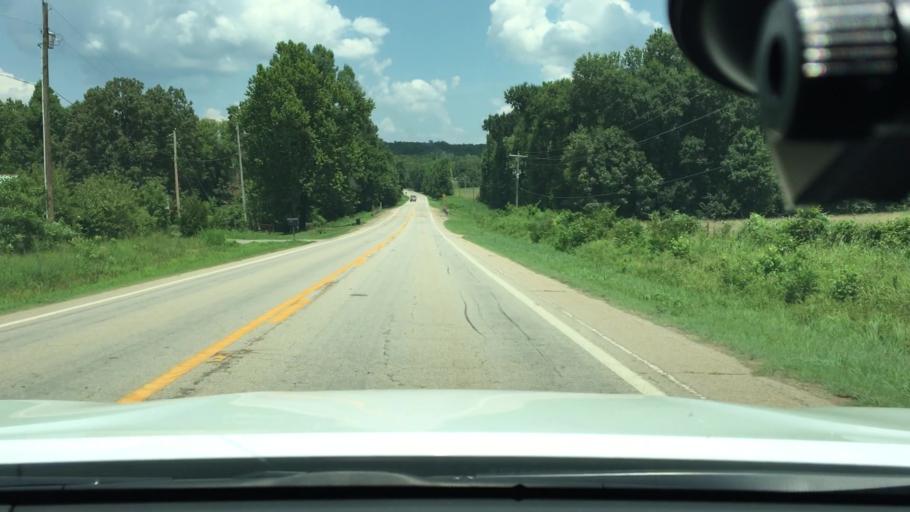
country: US
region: Arkansas
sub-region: Logan County
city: Booneville
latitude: 35.2035
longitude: -93.9243
